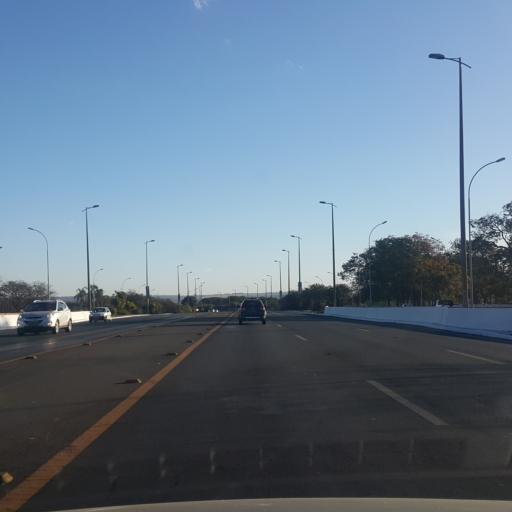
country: BR
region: Federal District
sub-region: Brasilia
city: Brasilia
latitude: -15.8355
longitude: -47.9265
